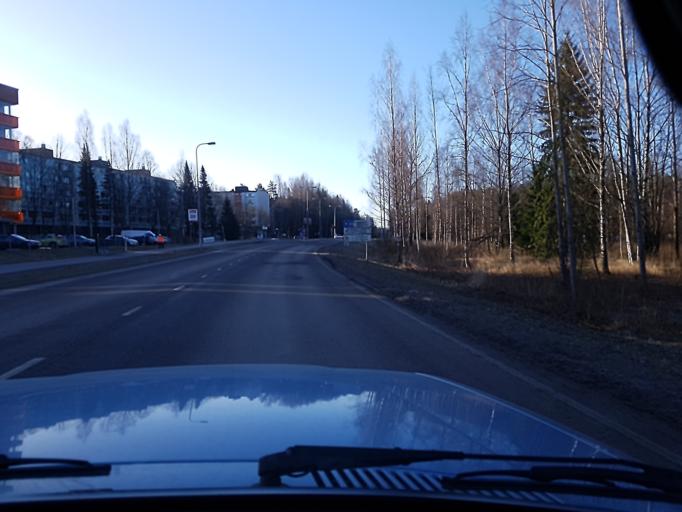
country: FI
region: Uusimaa
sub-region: Helsinki
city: Kilo
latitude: 60.2712
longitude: 24.8402
